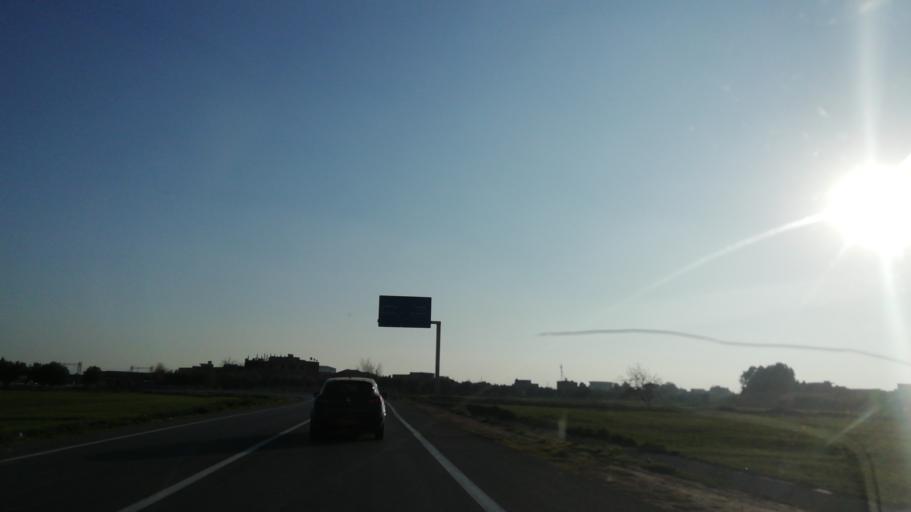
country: DZ
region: Sidi Bel Abbes
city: Sidi Bel Abbes
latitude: 35.1693
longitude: -0.6875
